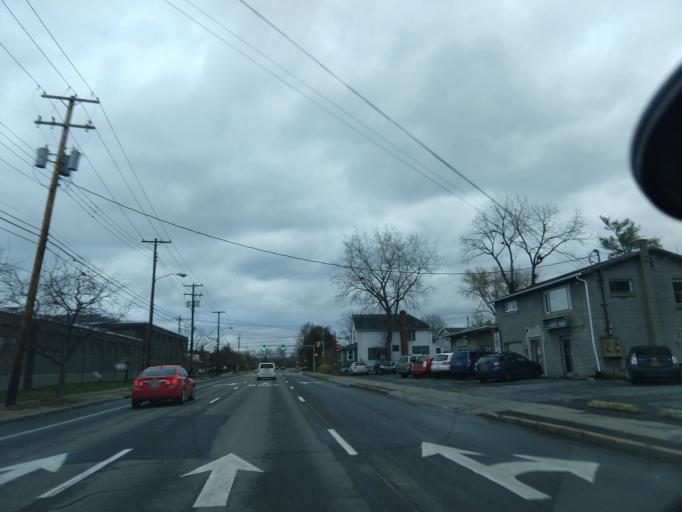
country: US
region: New York
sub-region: Tompkins County
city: Ithaca
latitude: 42.4434
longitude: -76.5086
